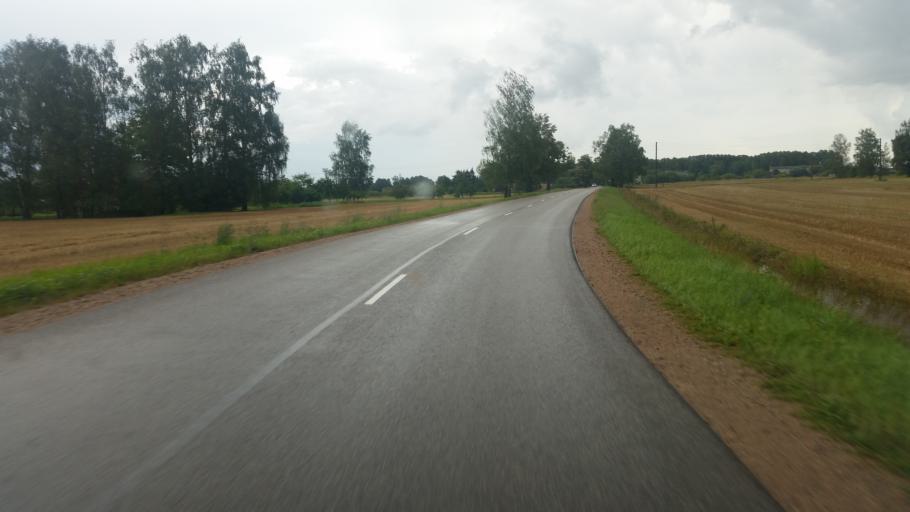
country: LV
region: Bauskas Rajons
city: Bauska
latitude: 56.4290
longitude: 24.3202
